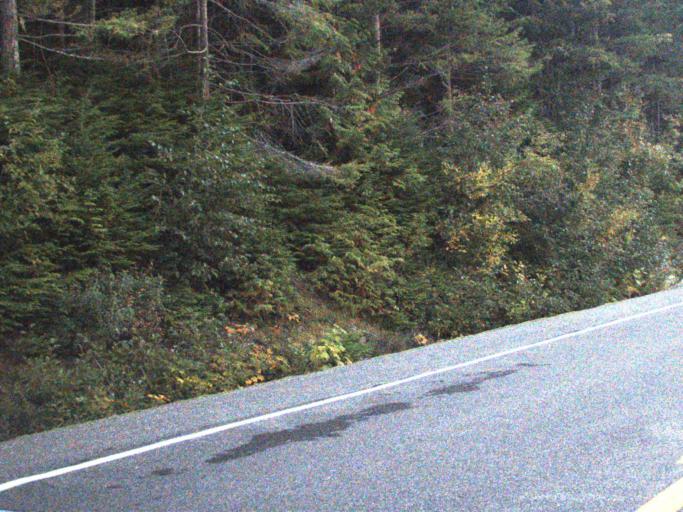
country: US
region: Washington
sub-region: Snohomish County
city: Darrington
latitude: 48.6650
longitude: -120.8715
